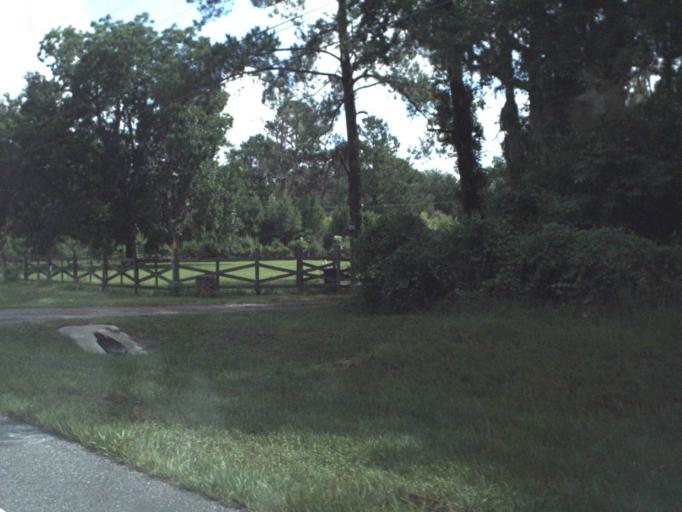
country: US
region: Florida
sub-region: Columbia County
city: Watertown
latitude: 30.0618
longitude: -82.5996
